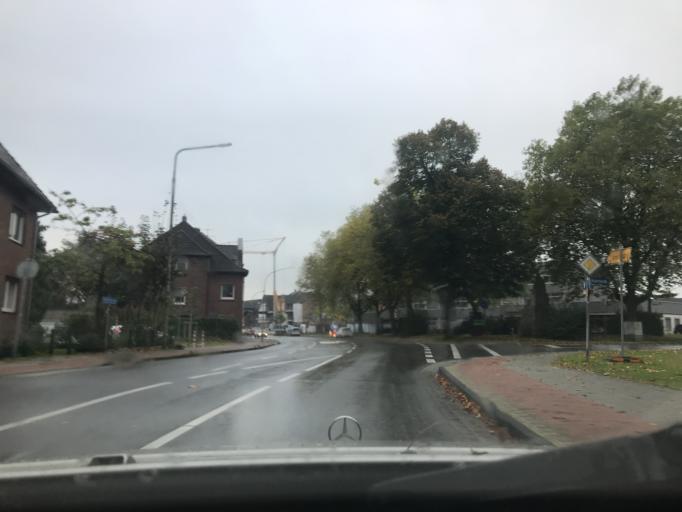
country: DE
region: North Rhine-Westphalia
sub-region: Regierungsbezirk Dusseldorf
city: Moers
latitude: 51.4500
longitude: 6.5805
